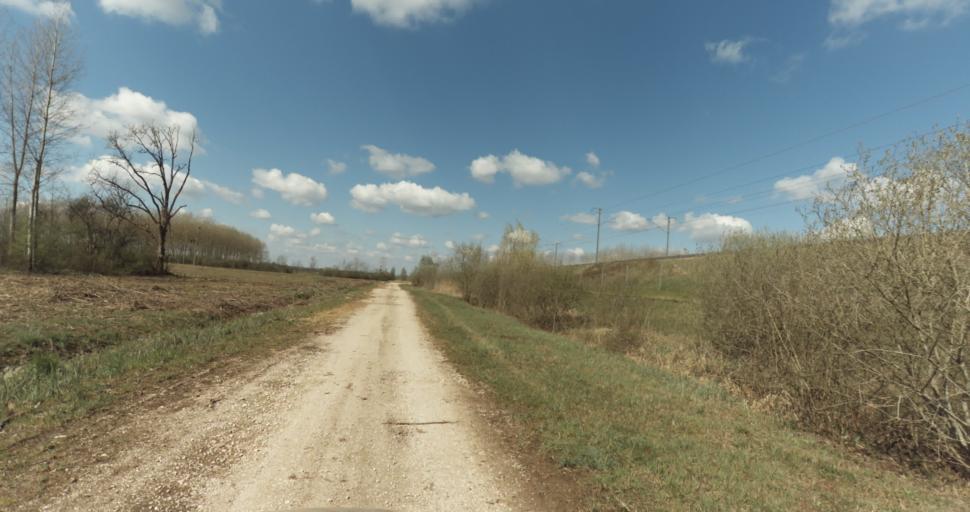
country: FR
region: Bourgogne
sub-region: Departement de la Cote-d'Or
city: Auxonne
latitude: 47.2235
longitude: 5.4186
